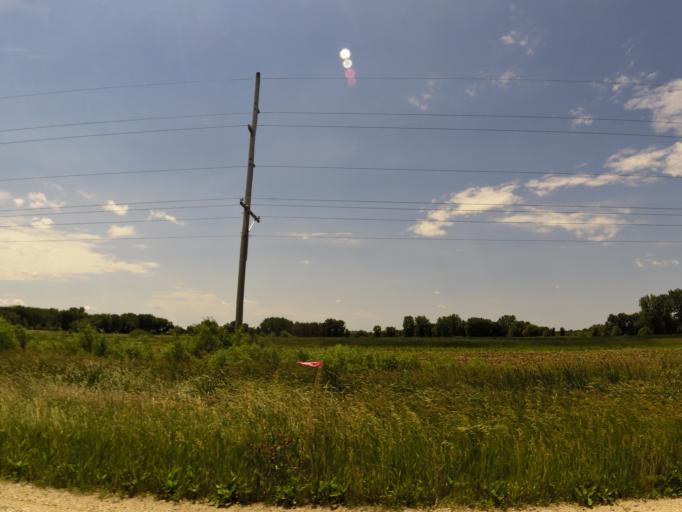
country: US
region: Iowa
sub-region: Buchanan County
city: Fairbank
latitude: 42.7148
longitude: -92.1588
